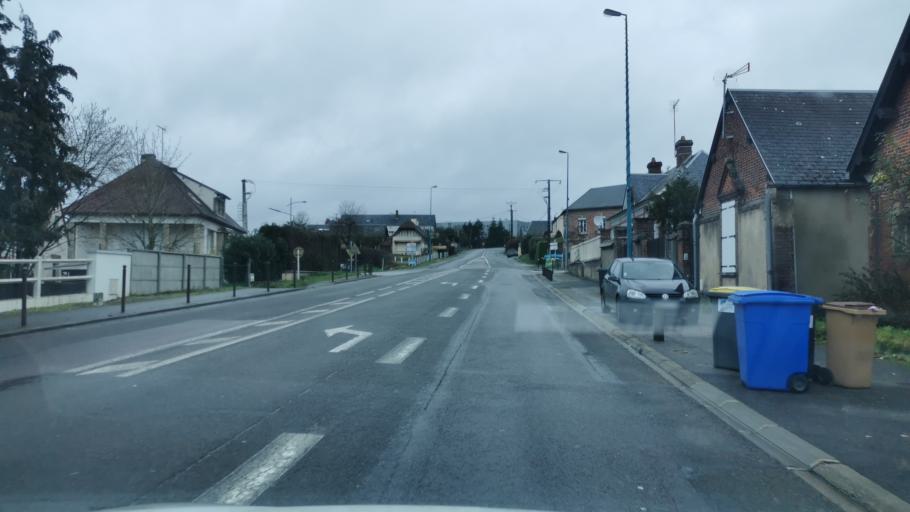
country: FR
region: Haute-Normandie
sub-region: Departement de l'Eure
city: Gravigny
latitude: 49.0662
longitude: 1.1728
